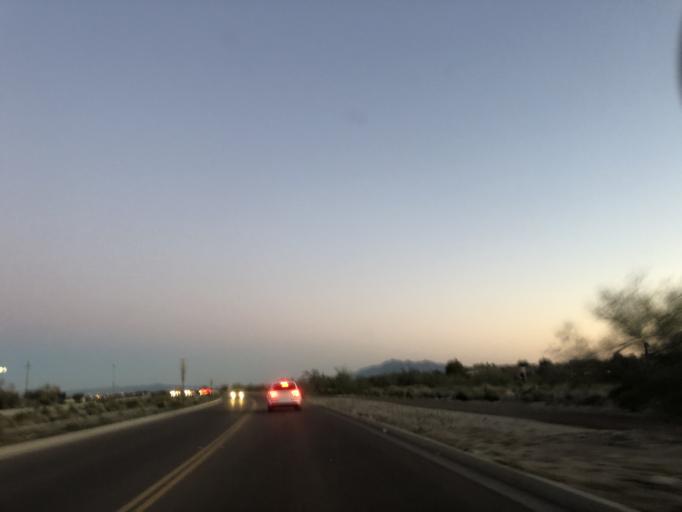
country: US
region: Arizona
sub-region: Maricopa County
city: Citrus Park
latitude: 33.4957
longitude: -112.4997
